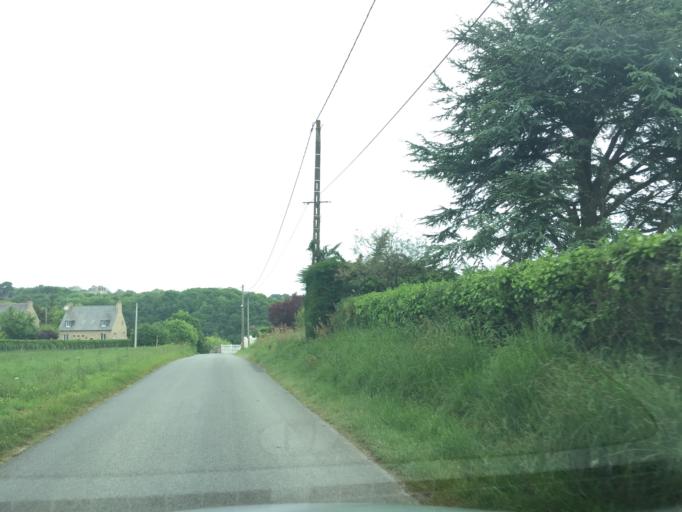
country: FR
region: Brittany
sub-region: Departement des Cotes-d'Armor
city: Crehen
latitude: 48.5921
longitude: -2.2221
